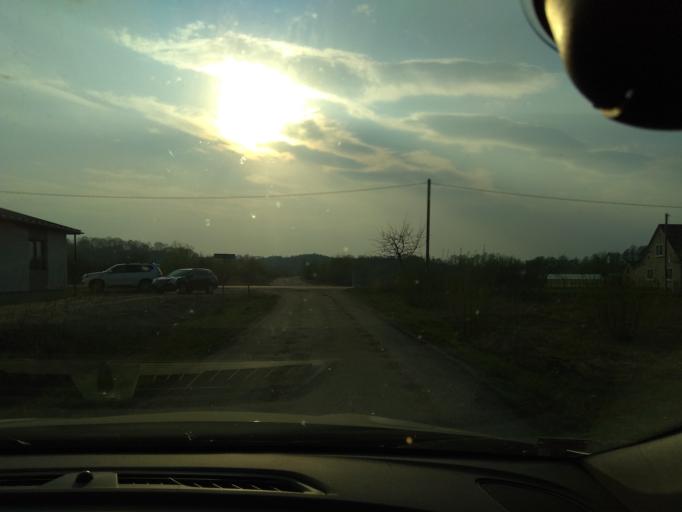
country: LT
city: Baltoji Voke
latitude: 54.5971
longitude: 25.1762
